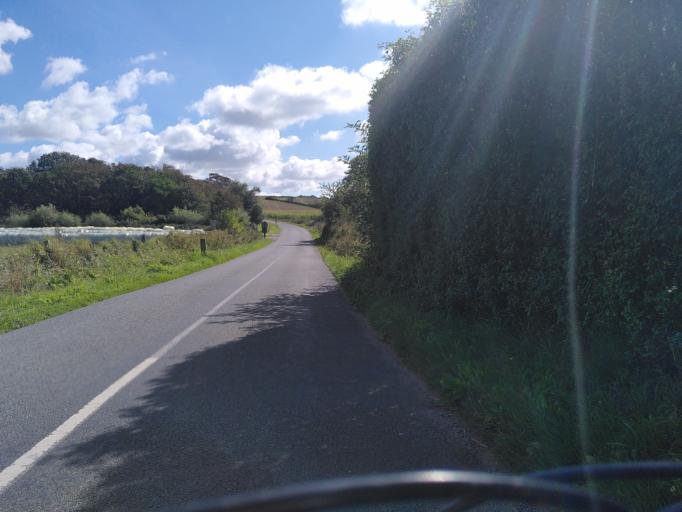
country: FR
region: Nord-Pas-de-Calais
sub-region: Departement du Pas-de-Calais
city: Wimille
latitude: 50.7797
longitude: 1.6282
